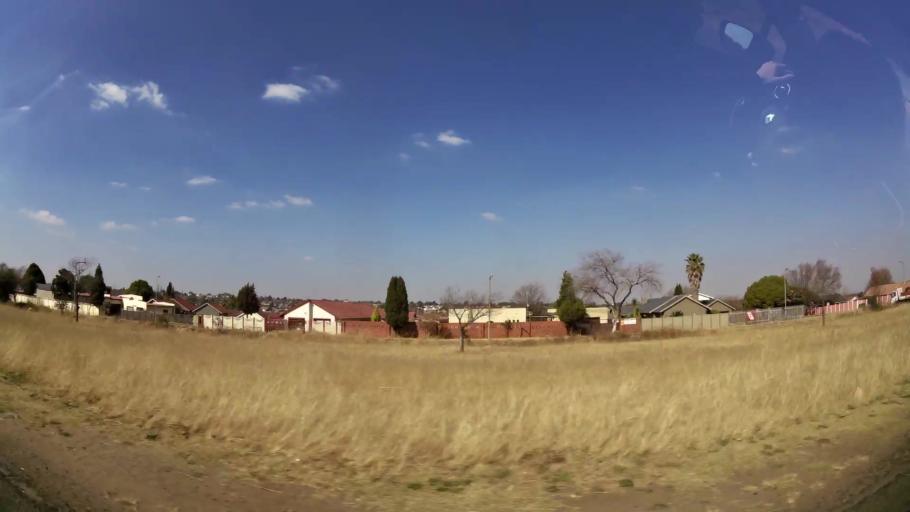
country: ZA
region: Gauteng
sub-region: City of Johannesburg Metropolitan Municipality
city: Roodepoort
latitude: -26.1407
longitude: 27.8166
